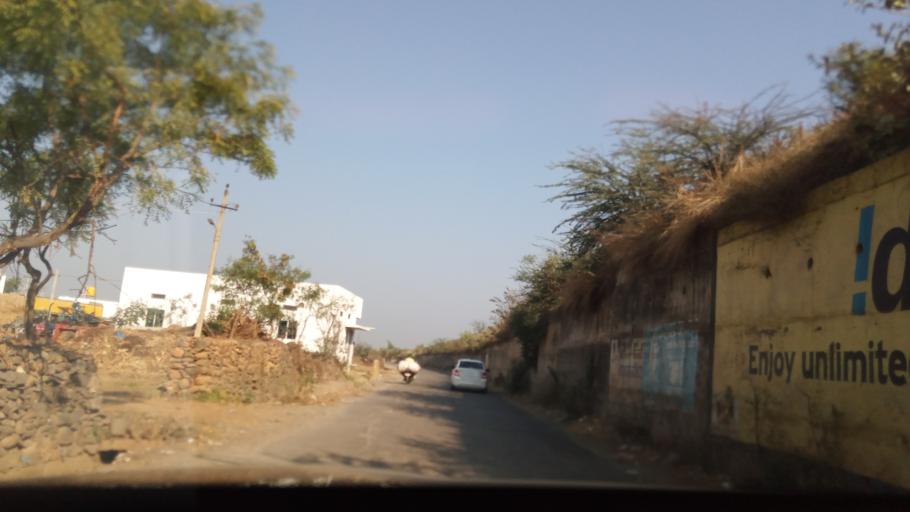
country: IN
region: Karnataka
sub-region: Haveri
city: Byadgi
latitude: 14.7191
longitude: 75.4812
